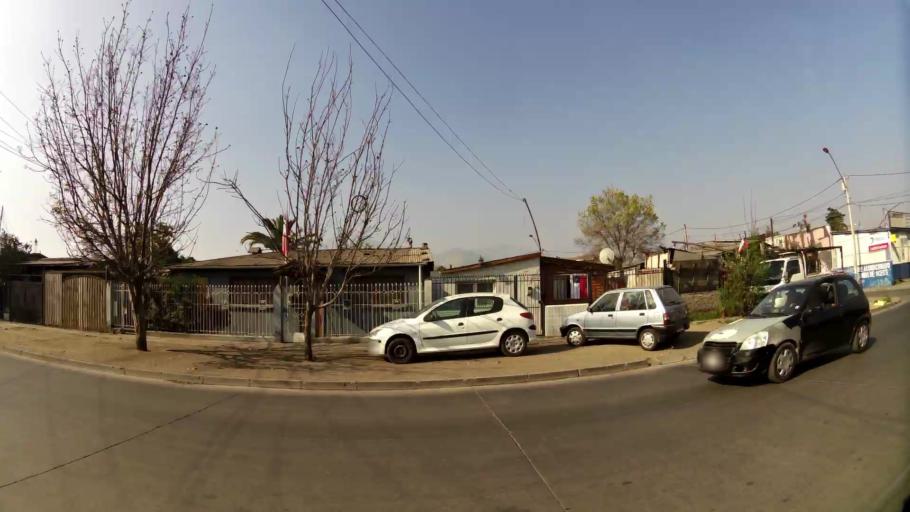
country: CL
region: Santiago Metropolitan
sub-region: Provincia de Santiago
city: Santiago
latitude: -33.3778
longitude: -70.6740
